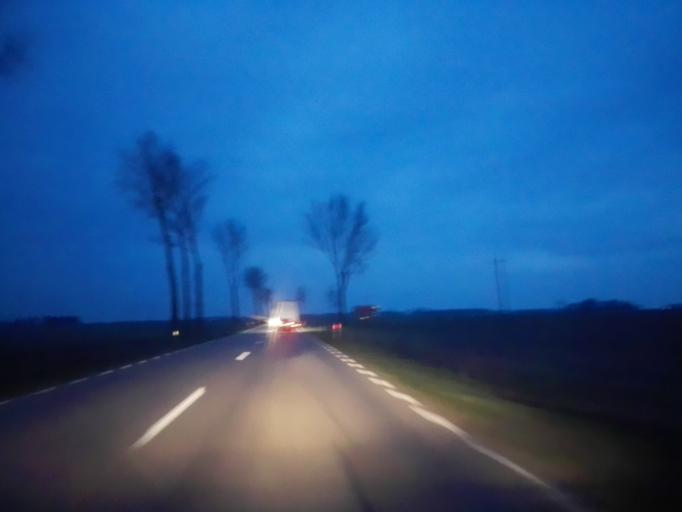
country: PL
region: Podlasie
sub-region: Powiat lomzynski
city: Sniadowo
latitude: 53.0863
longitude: 22.0205
